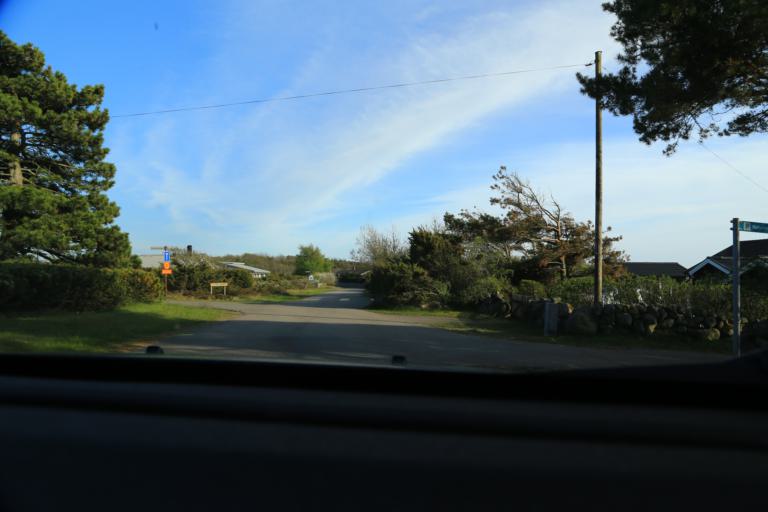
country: SE
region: Halland
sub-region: Varbergs Kommun
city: Traslovslage
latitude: 57.0422
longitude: 12.2927
